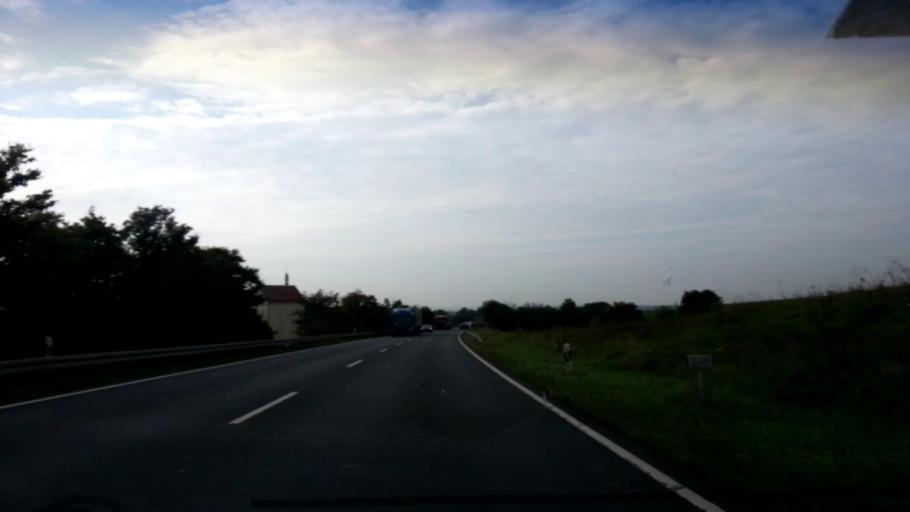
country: DE
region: Bavaria
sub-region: Regierungsbezirk Unterfranken
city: Lulsfeld
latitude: 49.8495
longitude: 10.3523
